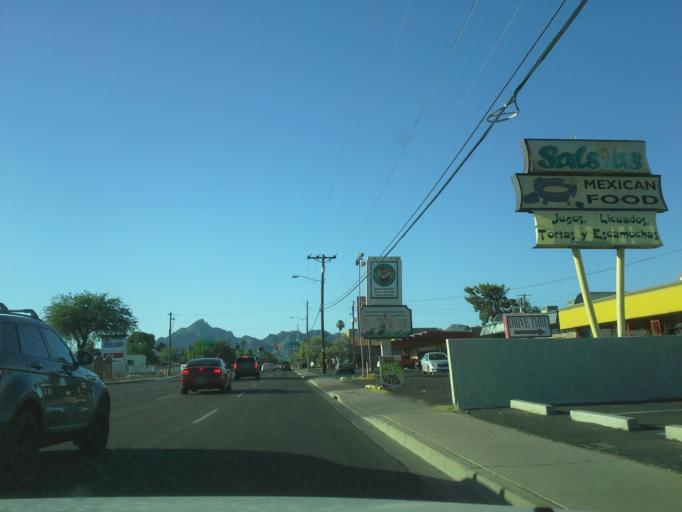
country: US
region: Arizona
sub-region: Maricopa County
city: Phoenix
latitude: 33.4935
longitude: -112.0129
